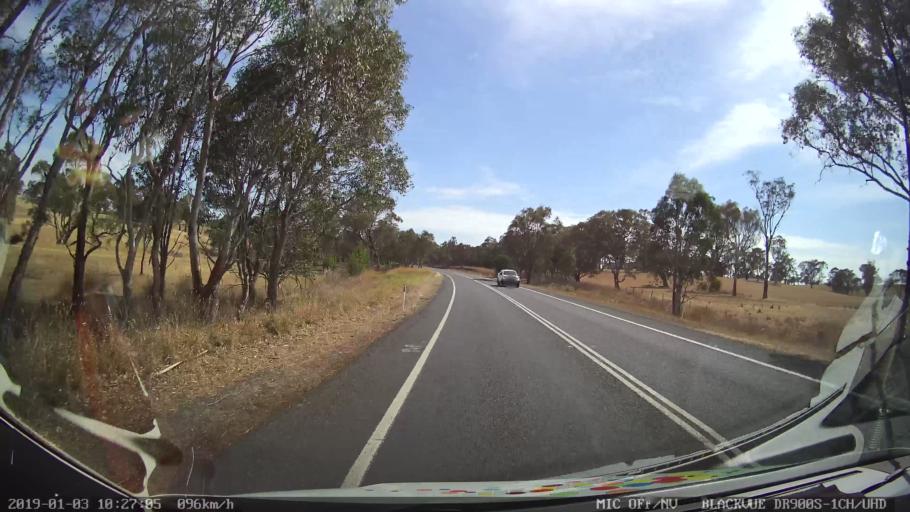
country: AU
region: New South Wales
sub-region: Young
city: Young
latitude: -34.4066
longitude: 148.2567
